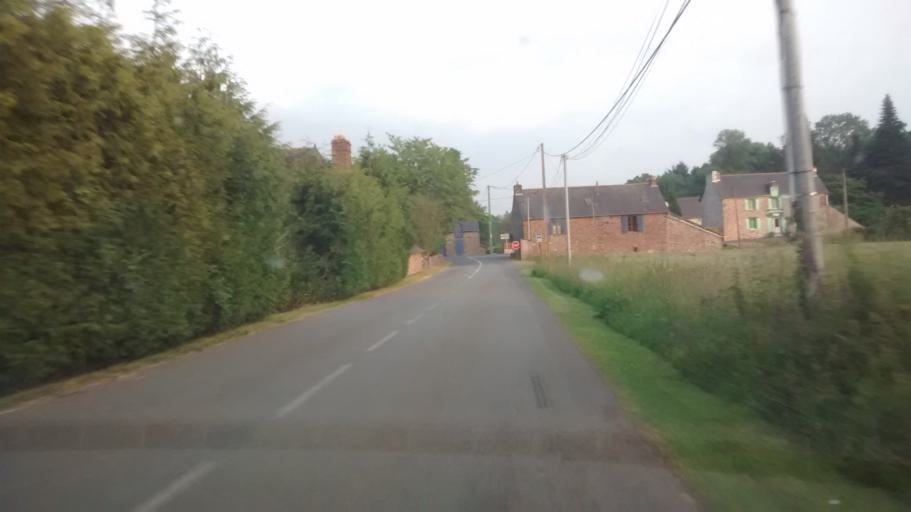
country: FR
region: Brittany
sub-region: Departement du Morbihan
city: Beignon
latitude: 47.9836
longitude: -2.1422
